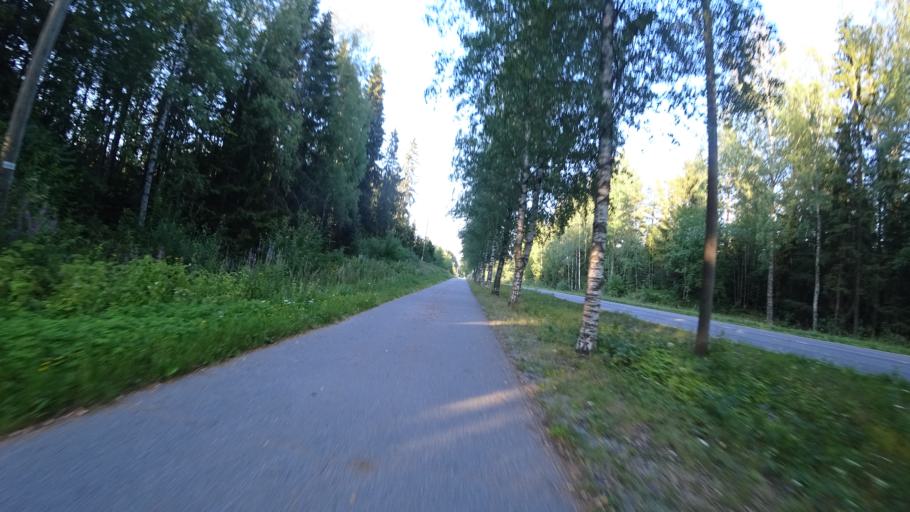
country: FI
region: Pirkanmaa
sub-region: Tampere
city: Nokia
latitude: 61.4710
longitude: 23.4608
